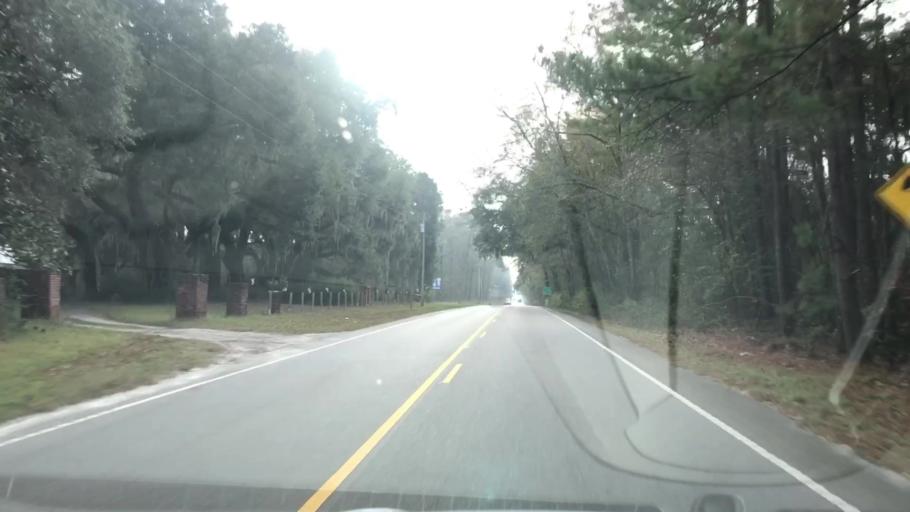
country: US
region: South Carolina
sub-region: Jasper County
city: Ridgeland
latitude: 32.5383
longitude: -80.9099
